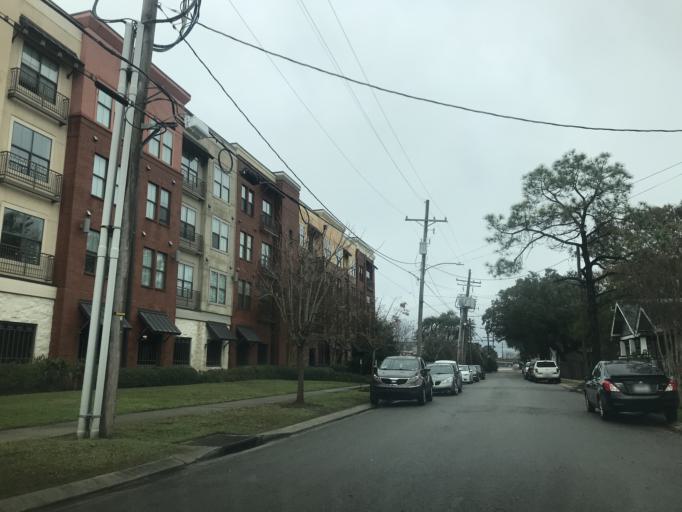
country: US
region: Louisiana
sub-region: Orleans Parish
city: New Orleans
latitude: 29.9712
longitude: -90.1079
